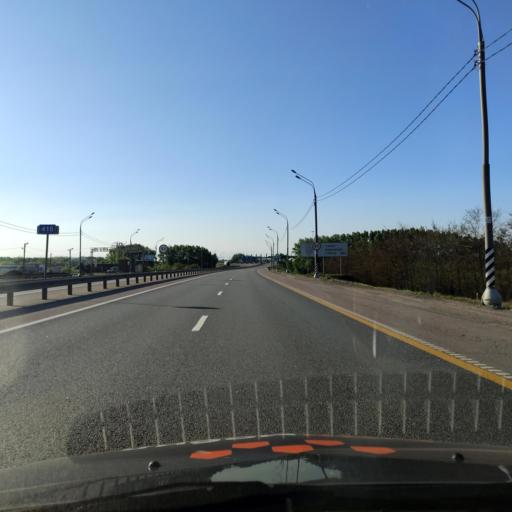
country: RU
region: Lipetsk
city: Zadonsk
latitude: 52.4338
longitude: 38.8193
